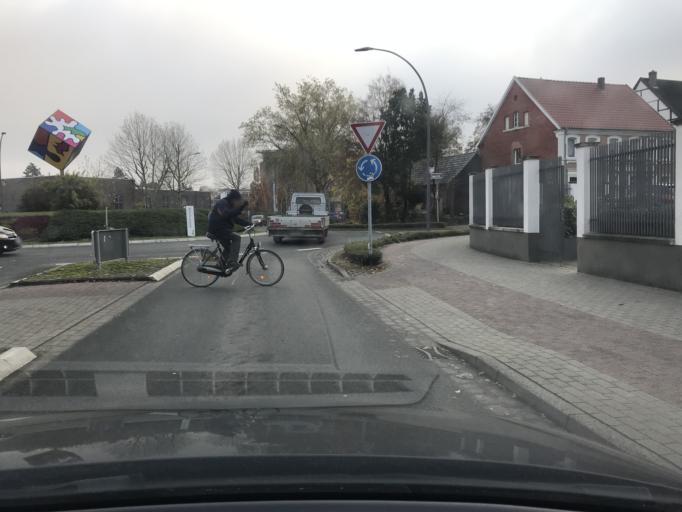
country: DE
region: North Rhine-Westphalia
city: Oelde
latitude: 51.8278
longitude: 8.1459
